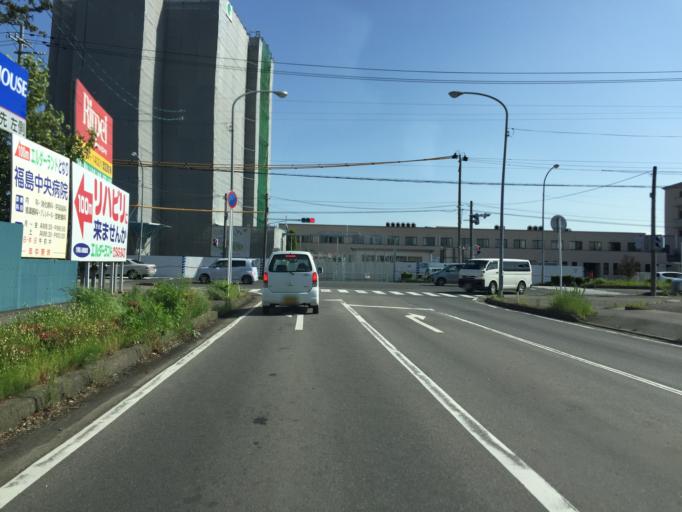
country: JP
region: Fukushima
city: Fukushima-shi
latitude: 37.7406
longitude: 140.4455
